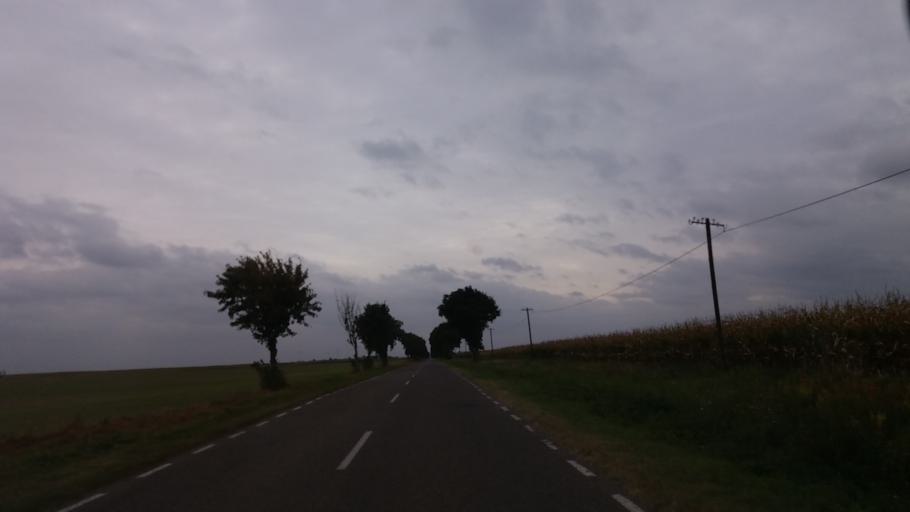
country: PL
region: Lubusz
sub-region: Powiat strzelecko-drezdenecki
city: Strzelce Krajenskie
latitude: 52.9564
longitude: 15.5743
